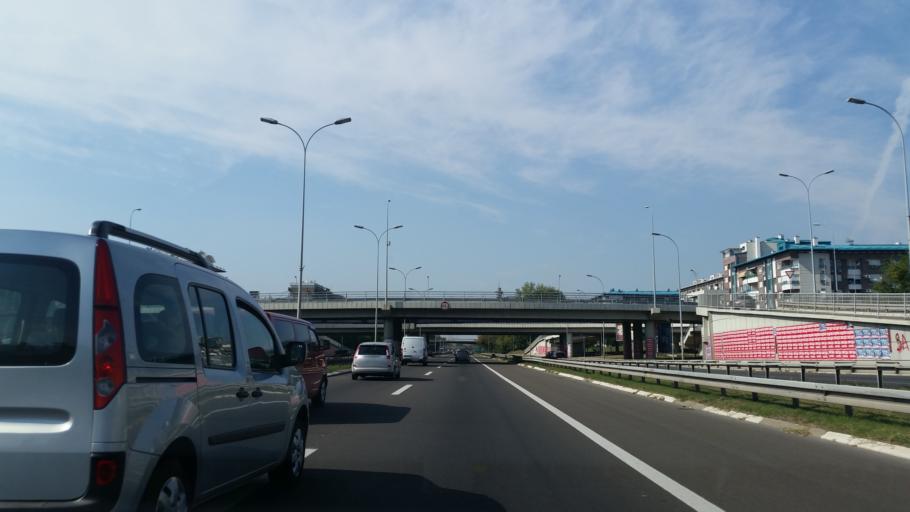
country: RS
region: Central Serbia
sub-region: Belgrade
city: Novi Beograd
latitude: 44.8127
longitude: 20.4198
